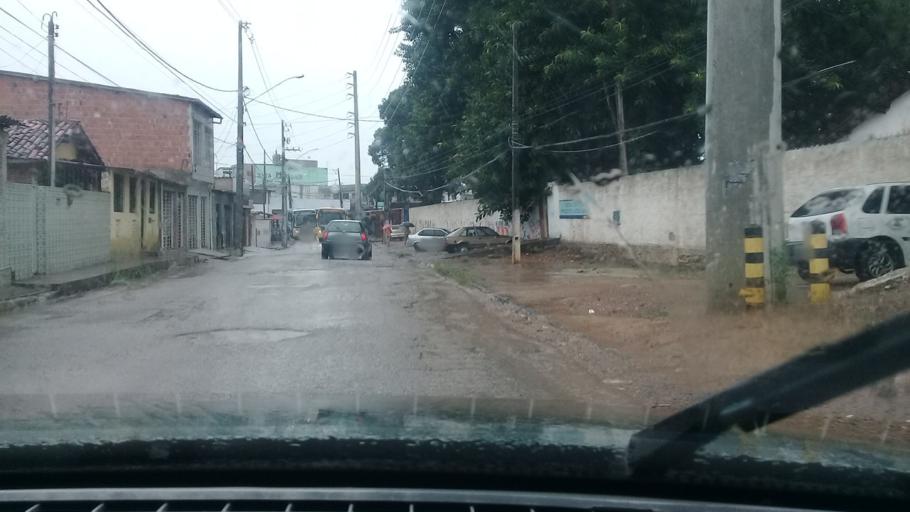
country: BR
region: Pernambuco
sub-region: Paulista
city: Paulista
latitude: -7.9581
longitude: -34.8909
